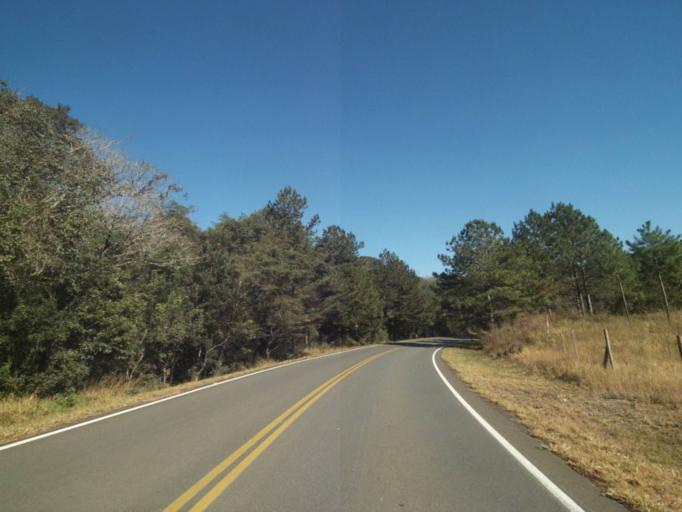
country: BR
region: Parana
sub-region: Telemaco Borba
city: Telemaco Borba
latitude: -24.4242
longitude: -50.5809
